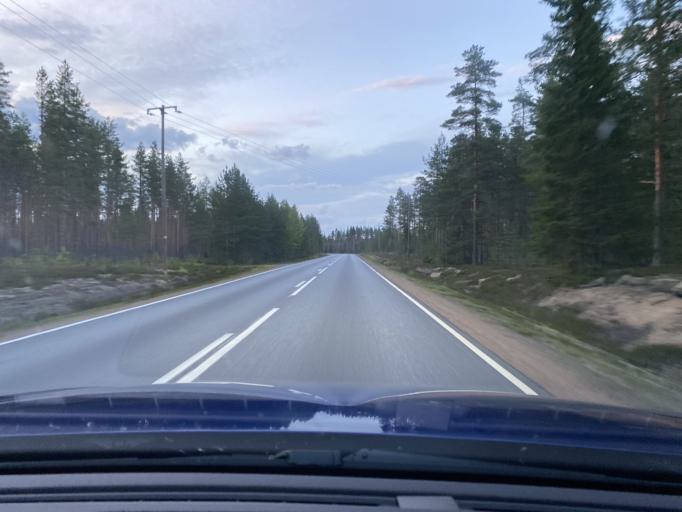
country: FI
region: Satakunta
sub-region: Pohjois-Satakunta
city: Honkajoki
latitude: 62.1898
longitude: 22.2970
